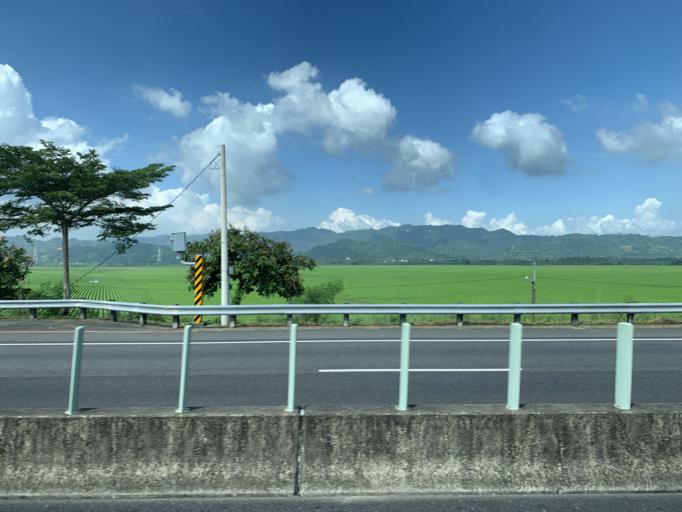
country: TW
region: Taiwan
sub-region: Pingtung
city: Pingtung
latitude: 22.8231
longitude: 120.4876
